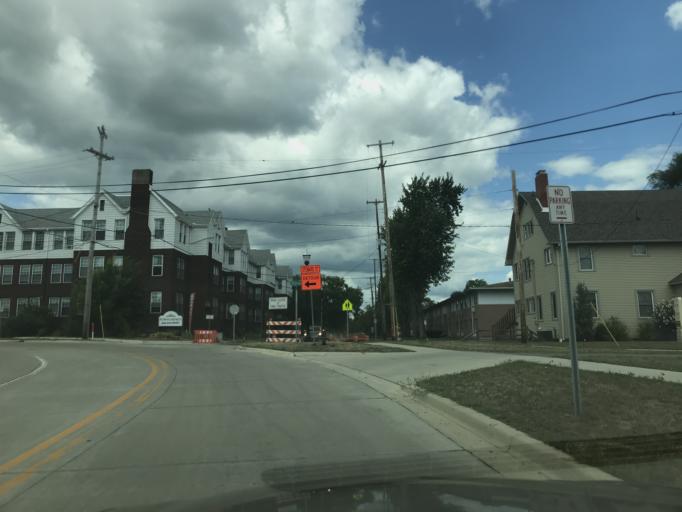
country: US
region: Michigan
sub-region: Jackson County
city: Jackson
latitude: 42.2480
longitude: -84.4162
